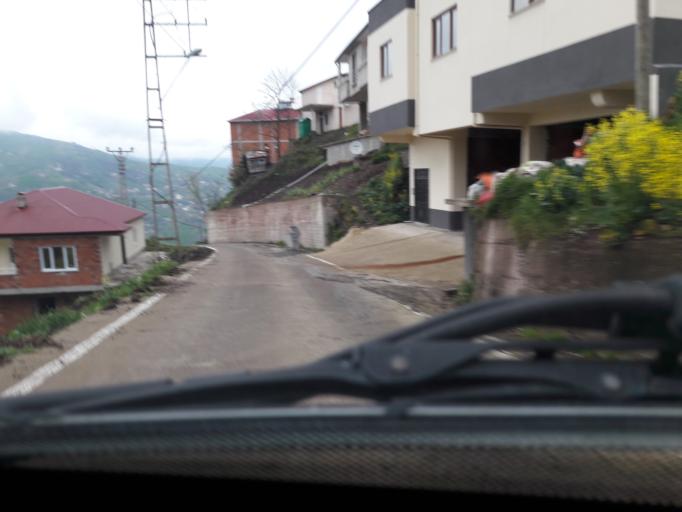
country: TR
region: Trabzon
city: Duzkoy
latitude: 40.8999
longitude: 39.4848
